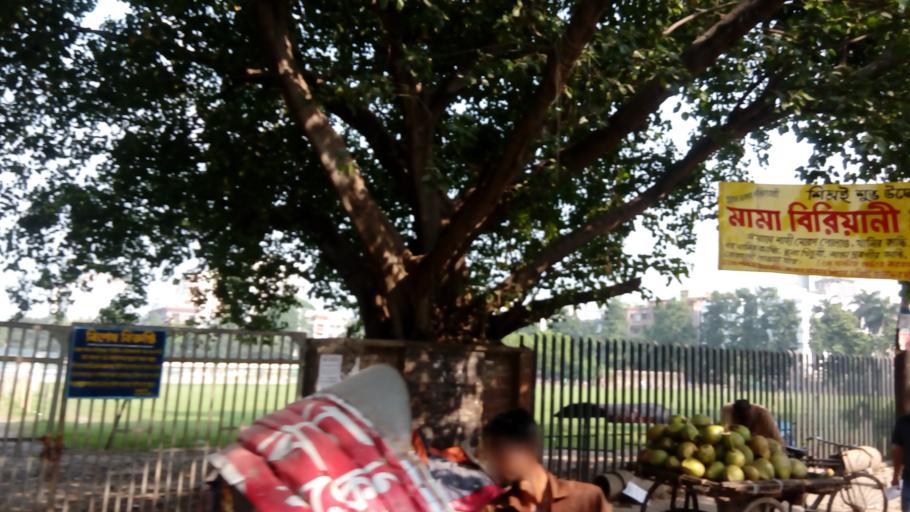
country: BD
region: Dhaka
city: Azimpur
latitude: 23.7487
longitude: 90.3697
